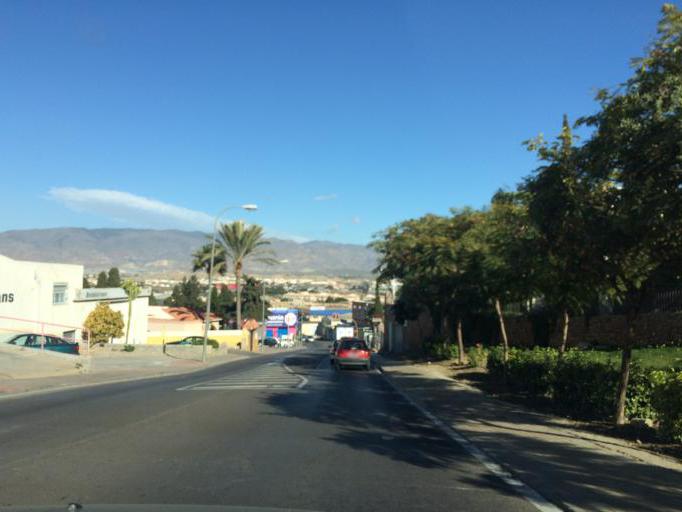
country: ES
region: Andalusia
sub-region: Provincia de Almeria
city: Huercal de Almeria
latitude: 36.8653
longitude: -2.4424
